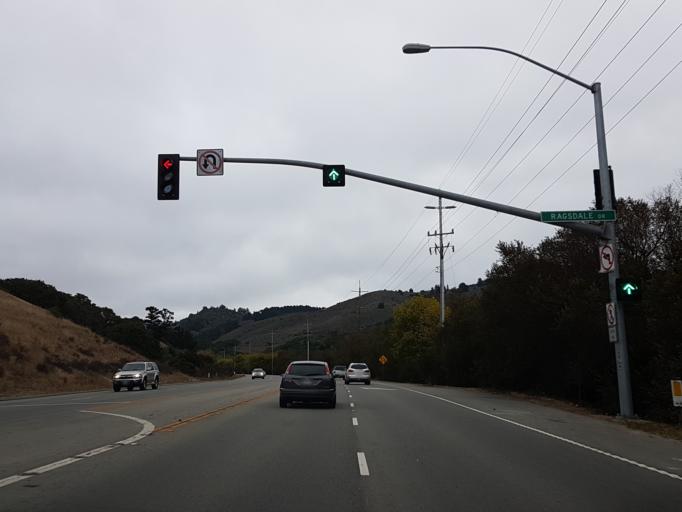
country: US
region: California
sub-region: Monterey County
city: Del Rey Oaks
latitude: 36.5780
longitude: -121.8253
